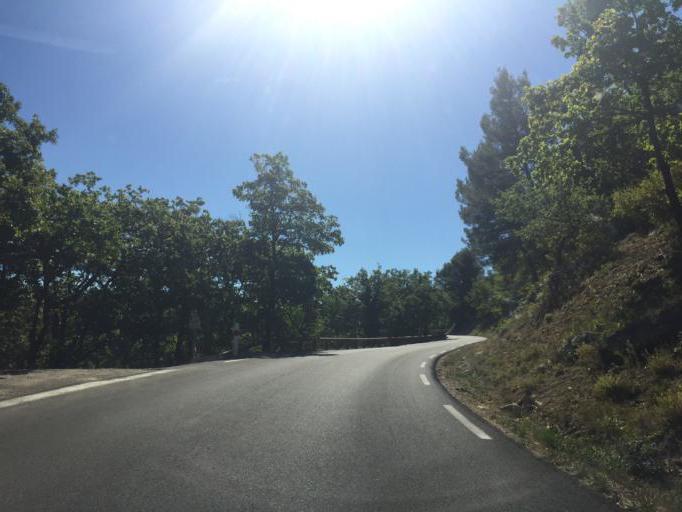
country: FR
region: Provence-Alpes-Cote d'Azur
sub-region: Departement du Vaucluse
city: Venasque
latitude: 43.9965
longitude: 5.1518
